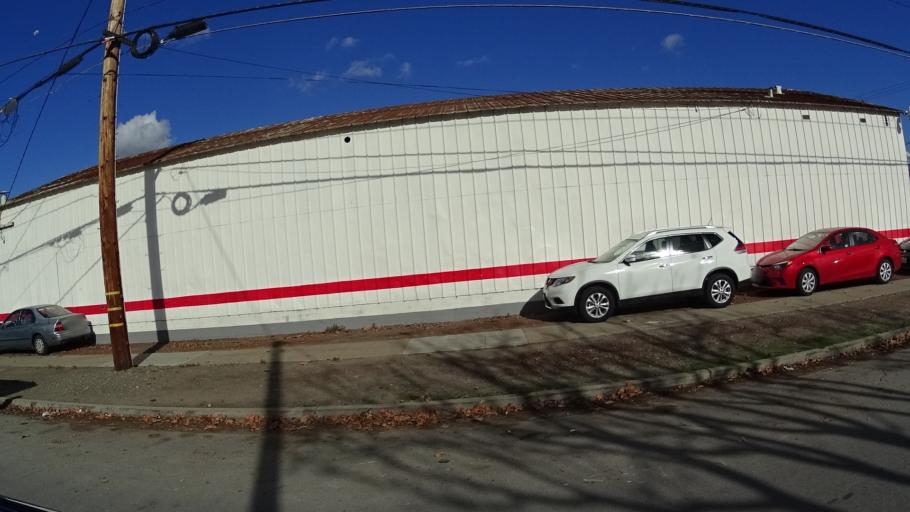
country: US
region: California
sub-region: Santa Clara County
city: San Jose
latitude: 37.3436
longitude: -121.9145
